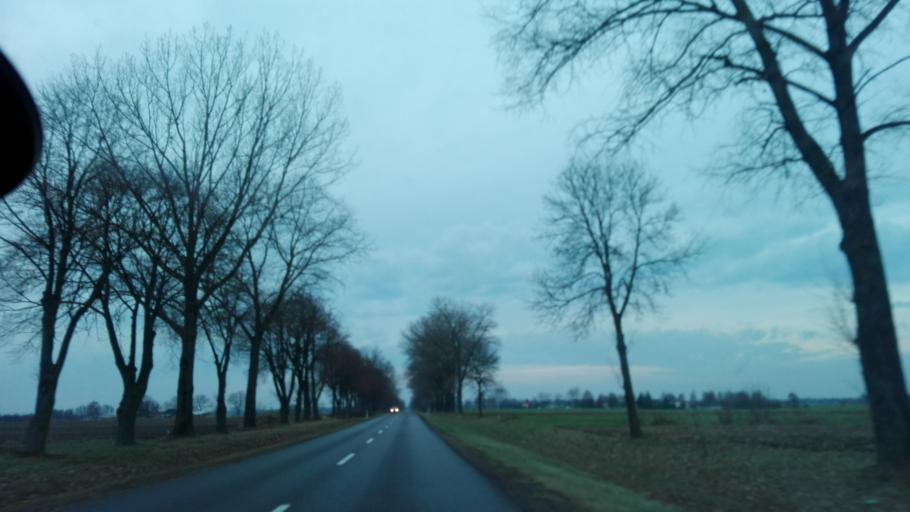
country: PL
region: Lublin Voivodeship
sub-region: Powiat radzynski
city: Wohyn
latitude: 51.7788
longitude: 22.7991
